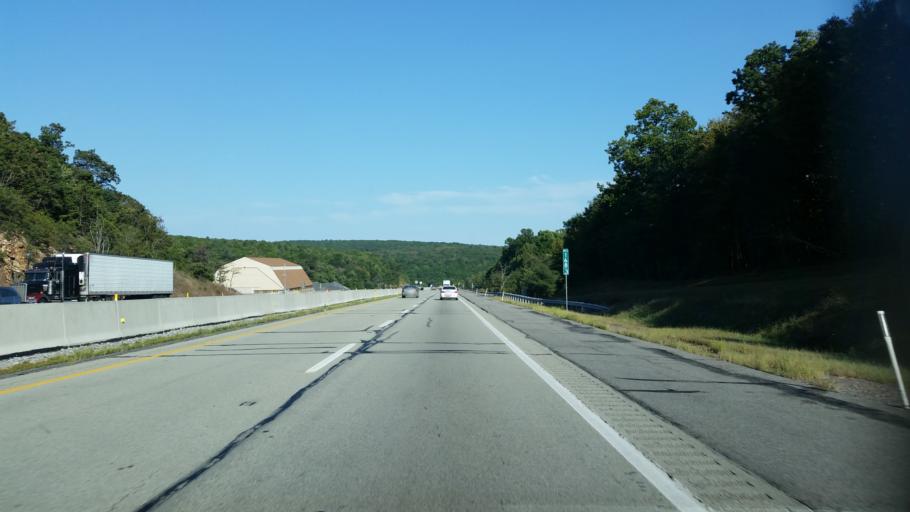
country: US
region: Pennsylvania
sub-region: Fulton County
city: McConnellsburg
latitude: 40.0338
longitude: -78.1465
